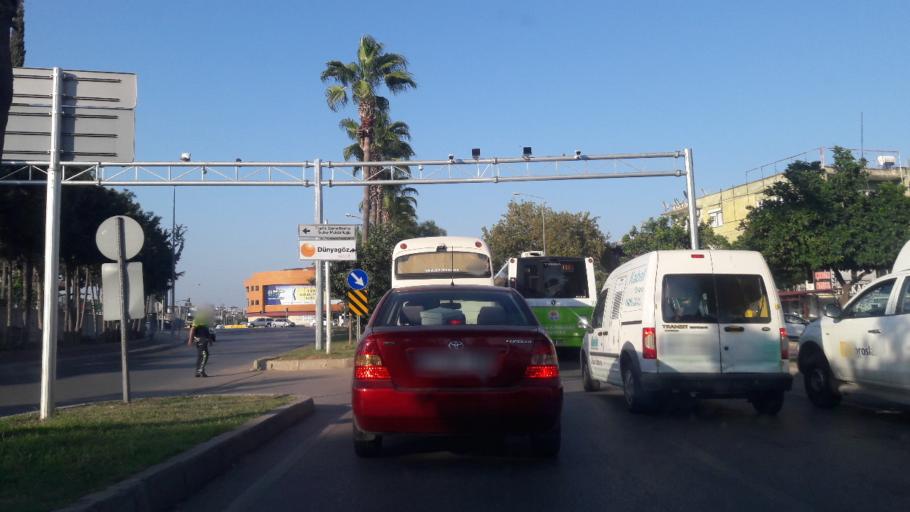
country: TR
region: Adana
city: Seyhan
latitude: 36.9923
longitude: 35.2993
